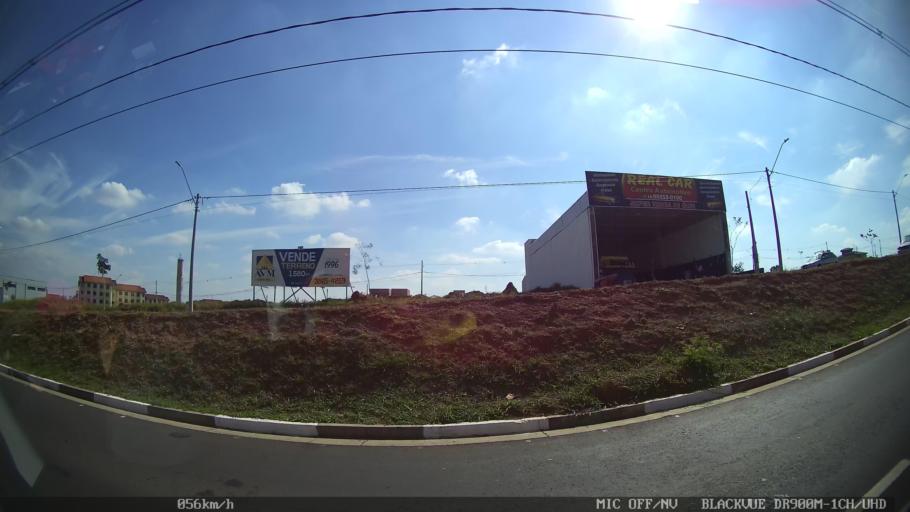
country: BR
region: Sao Paulo
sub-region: Hortolandia
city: Hortolandia
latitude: -22.8528
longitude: -47.2188
